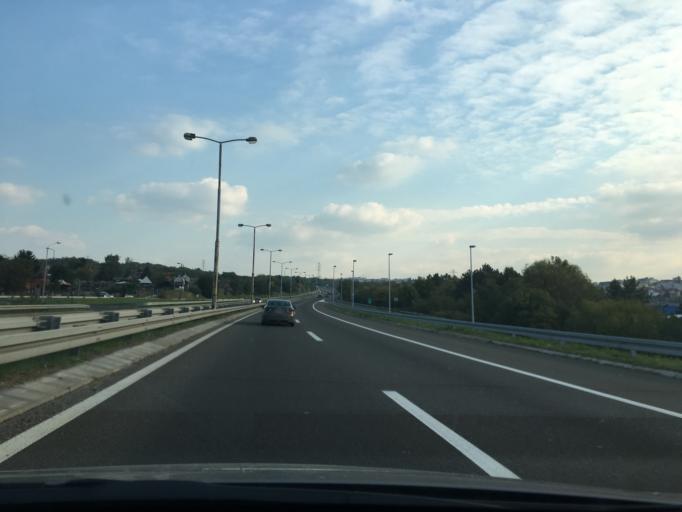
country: RS
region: Central Serbia
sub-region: Belgrade
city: Zvezdara
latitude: 44.7723
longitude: 20.5196
